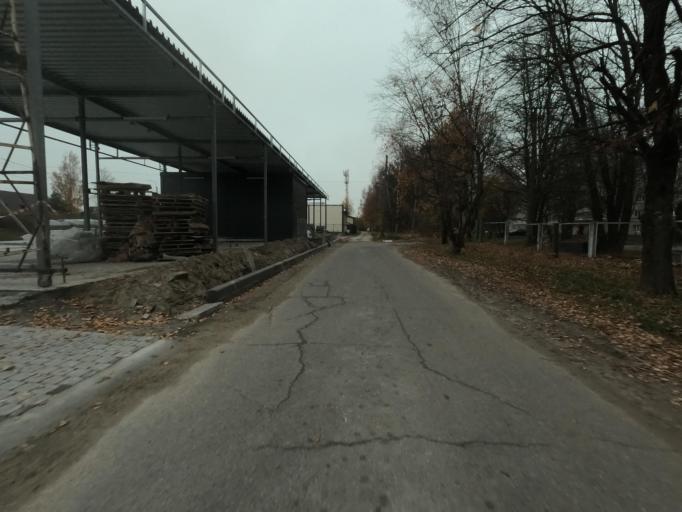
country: RU
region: Leningrad
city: Kirovsk
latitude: 59.8986
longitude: 30.9978
